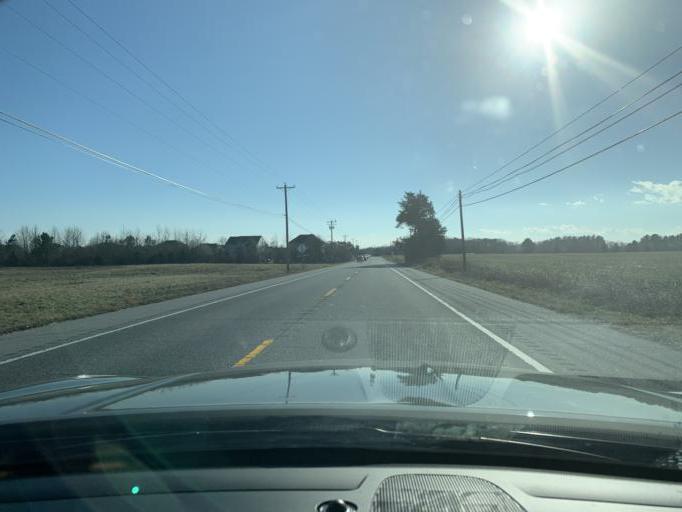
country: US
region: Maryland
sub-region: Queen Anne's County
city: Centreville
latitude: 39.0664
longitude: -76.0503
